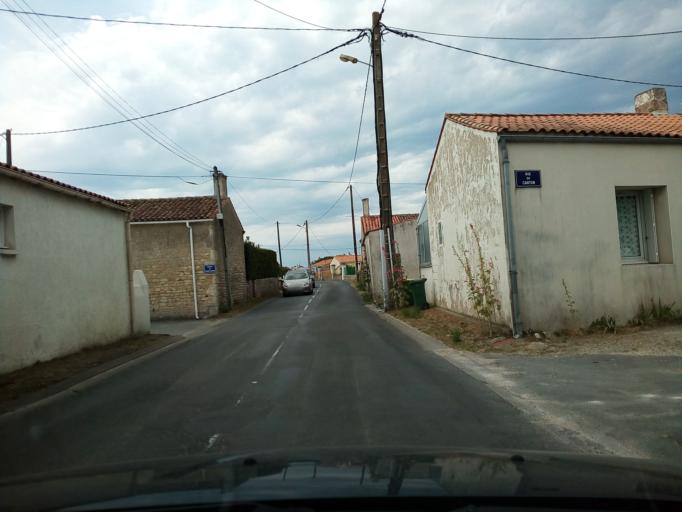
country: FR
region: Poitou-Charentes
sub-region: Departement de la Charente-Maritime
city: Dolus-d'Oleron
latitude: 45.9254
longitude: -1.3225
